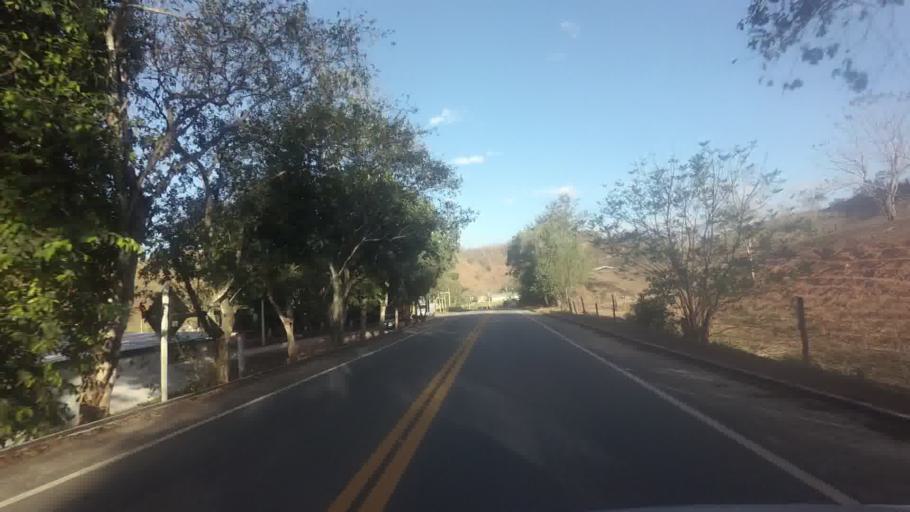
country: BR
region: Espirito Santo
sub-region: Cachoeiro De Itapemirim
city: Cachoeiro de Itapemirim
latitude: -20.8290
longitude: -41.2078
